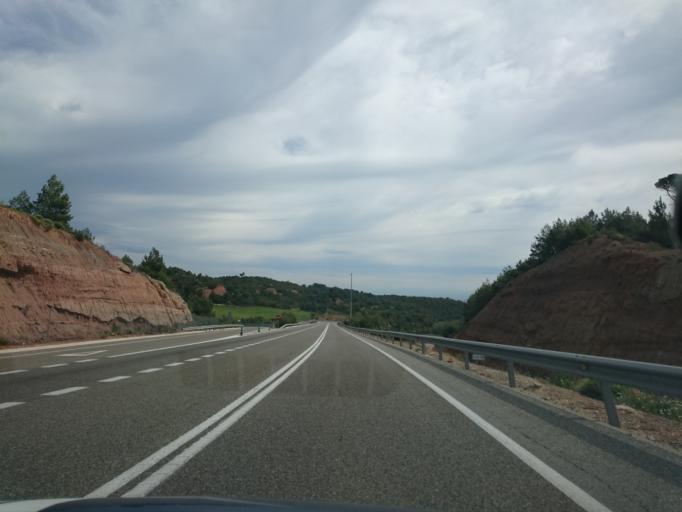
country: ES
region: Catalonia
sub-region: Provincia de Barcelona
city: Castellfollit del Boix
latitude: 41.6568
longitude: 1.7202
